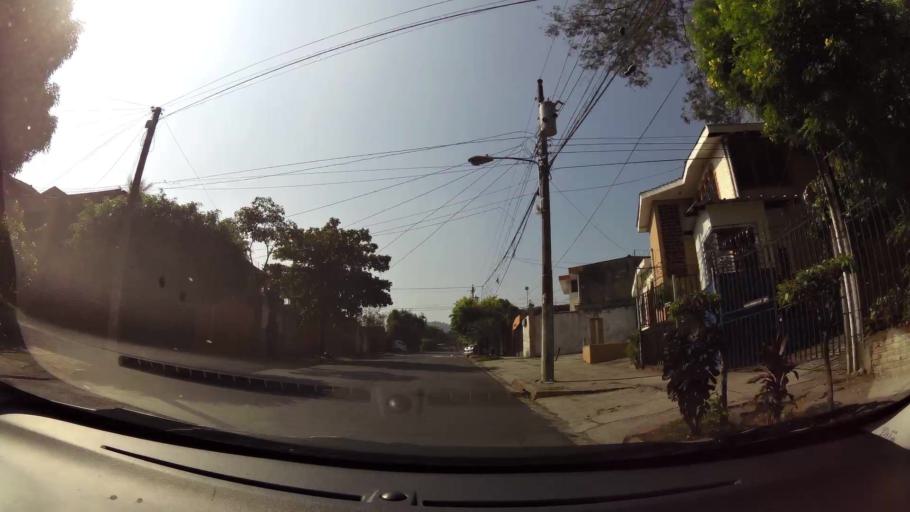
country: SV
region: La Libertad
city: Antiguo Cuscatlan
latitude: 13.6743
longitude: -89.2395
